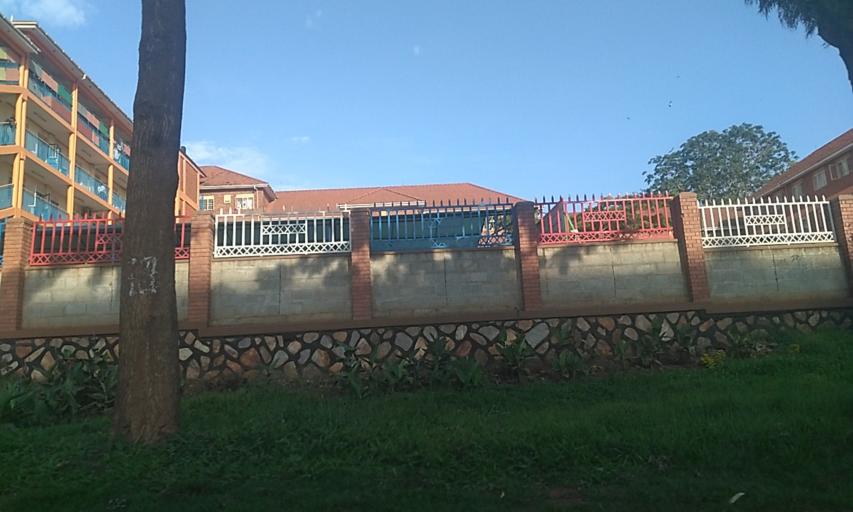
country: UG
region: Central Region
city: Kampala Central Division
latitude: 0.3280
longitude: 32.5743
